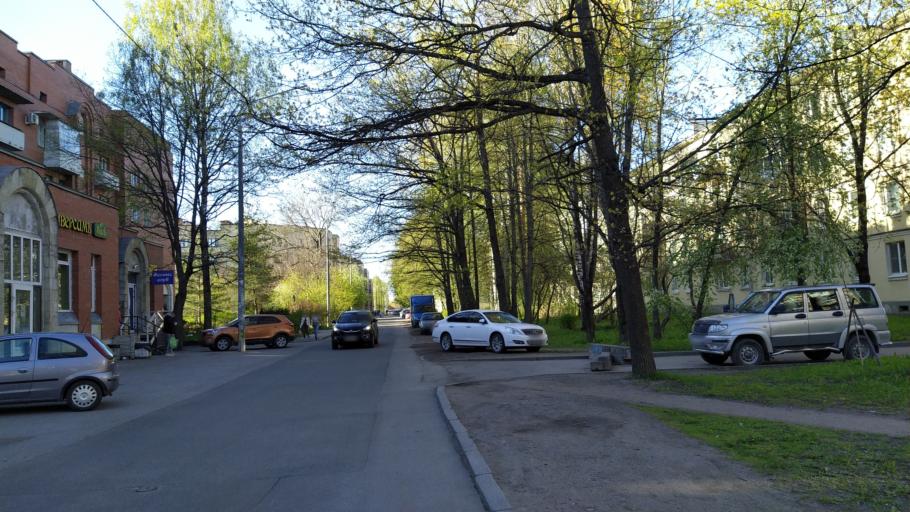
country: RU
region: St.-Petersburg
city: Pavlovsk
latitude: 59.6870
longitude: 30.4286
